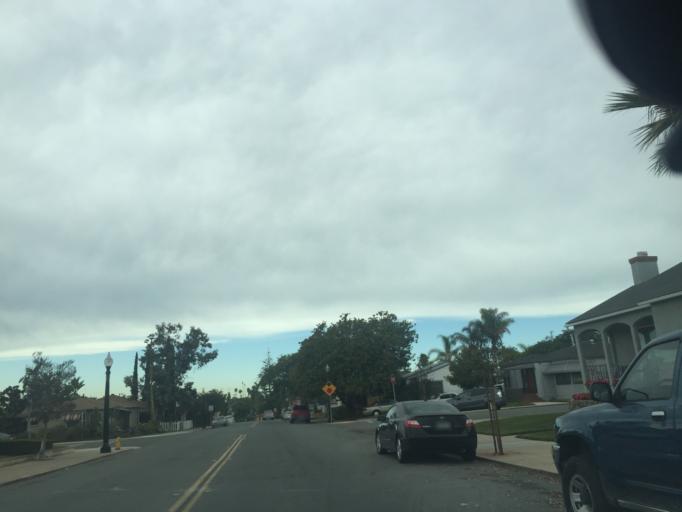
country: US
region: California
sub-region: San Diego County
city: Lemon Grove
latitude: 32.7593
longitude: -117.0905
